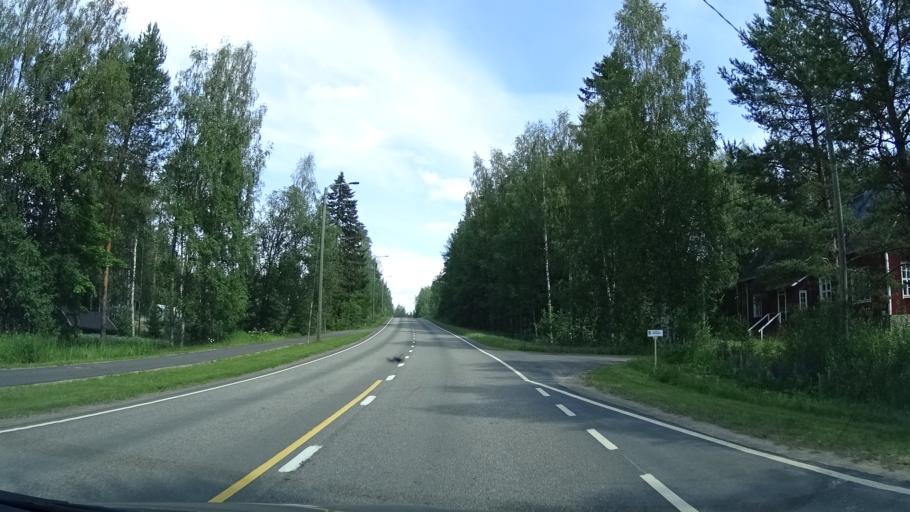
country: FI
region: Central Finland
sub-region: Keuruu
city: Multia
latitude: 62.4125
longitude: 24.8170
